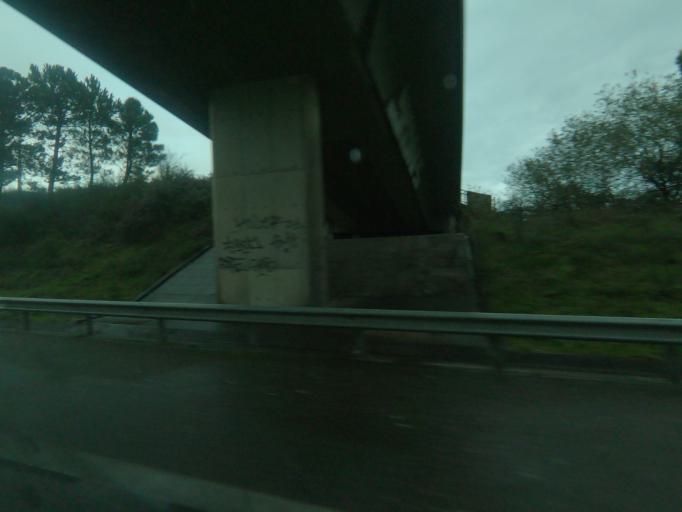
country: PT
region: Viana do Castelo
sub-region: Vila Nova de Cerveira
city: Vila Nova de Cerveira
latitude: 41.9462
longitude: -8.6659
